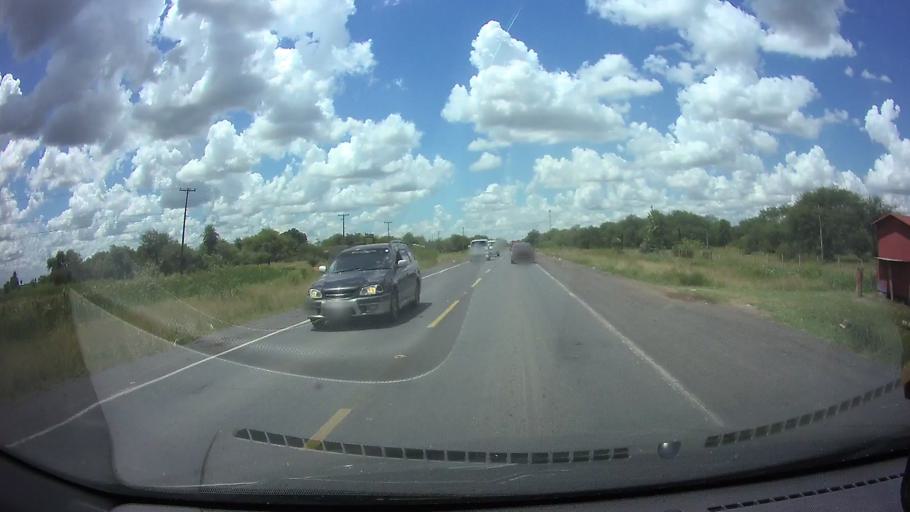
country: PY
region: Presidente Hayes
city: Nanawa
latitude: -25.2280
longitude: -57.6885
